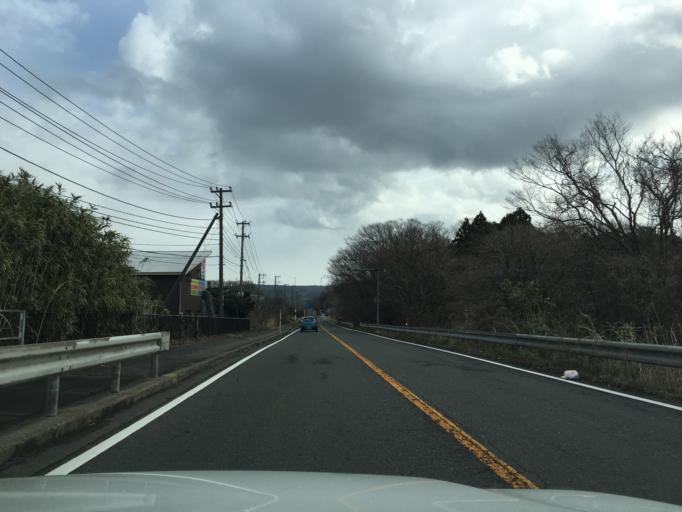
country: JP
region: Yamagata
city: Yuza
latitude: 39.2817
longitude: 139.9397
